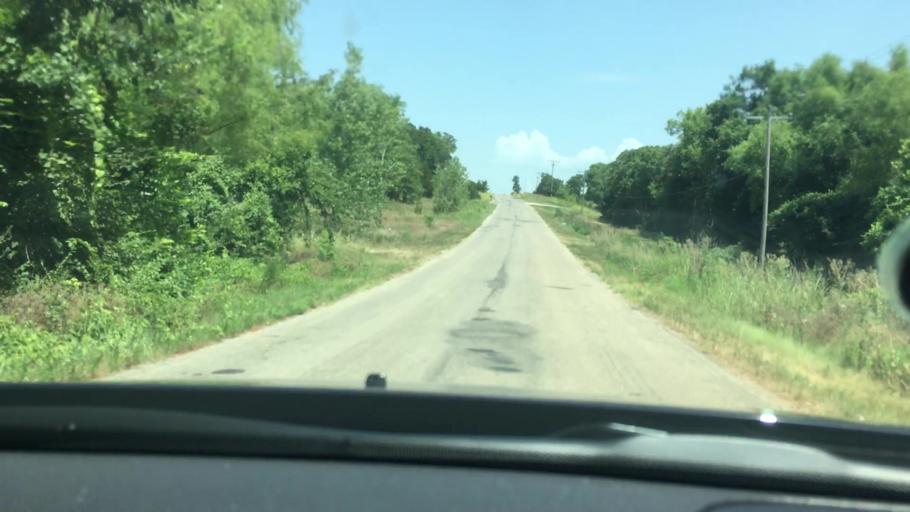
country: US
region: Oklahoma
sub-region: Pontotoc County
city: Byng
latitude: 34.8411
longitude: -96.6698
